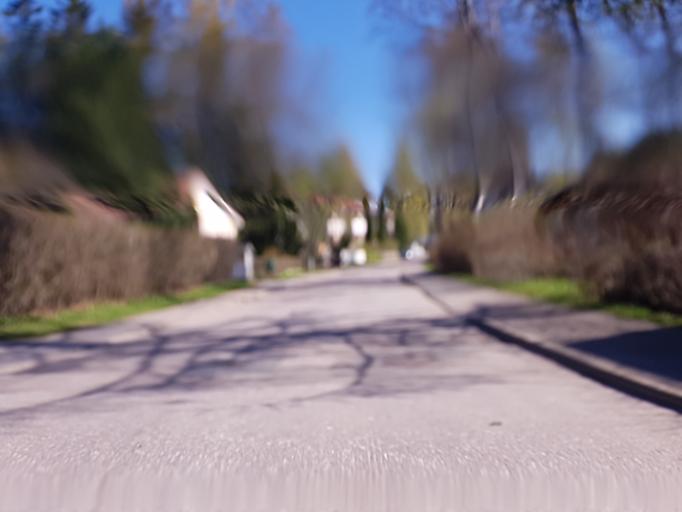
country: FI
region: Uusimaa
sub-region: Helsinki
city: Helsinki
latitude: 60.2505
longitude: 24.9353
